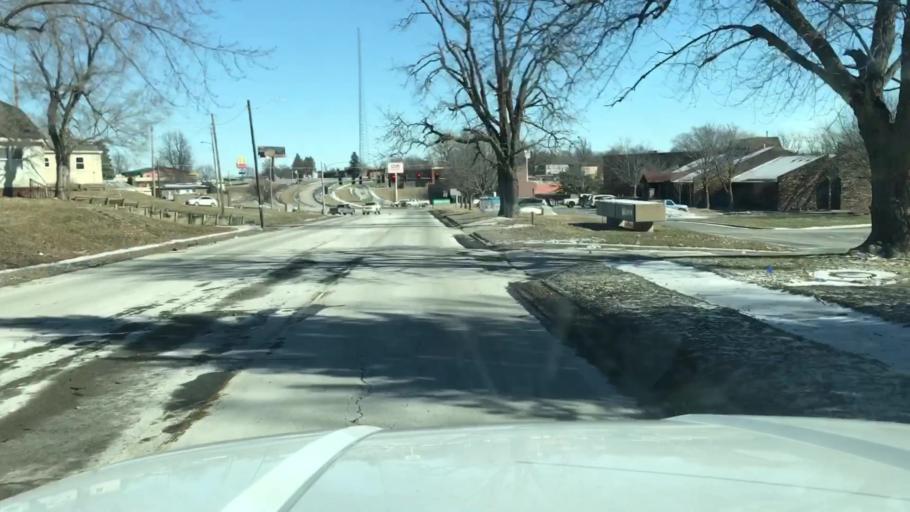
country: US
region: Missouri
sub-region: Andrew County
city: Country Club Village
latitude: 39.7985
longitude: -94.8189
